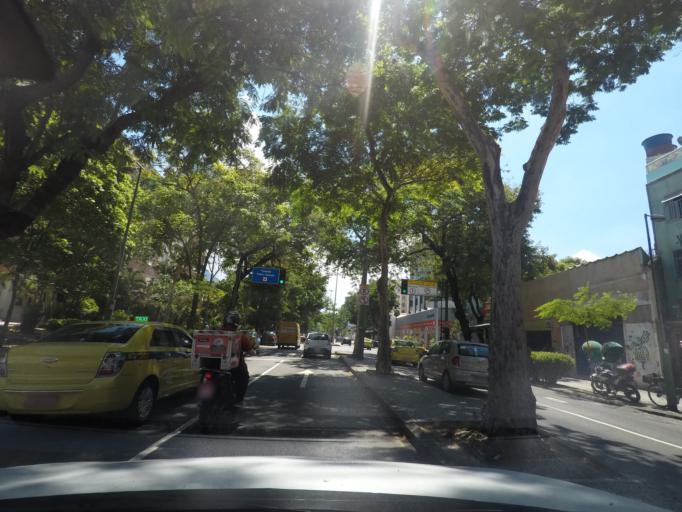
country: BR
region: Rio de Janeiro
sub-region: Rio De Janeiro
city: Rio de Janeiro
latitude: -22.9140
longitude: -43.2368
